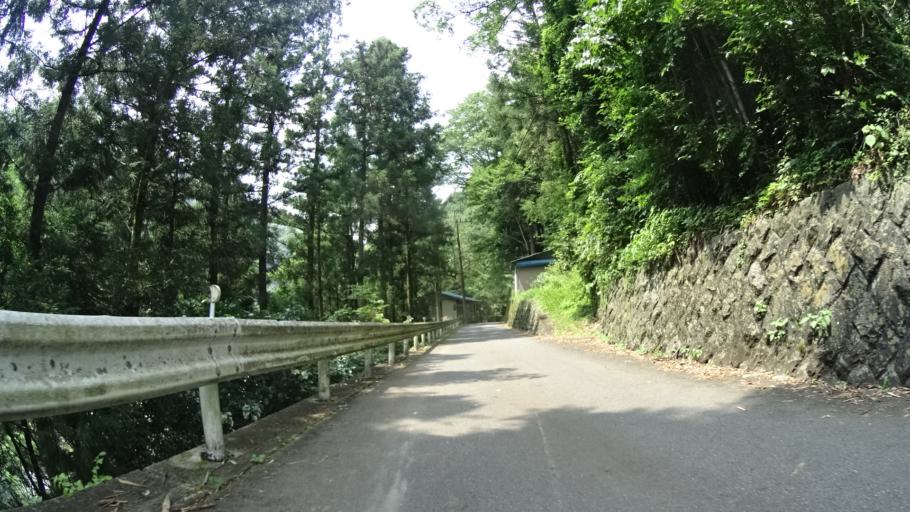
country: JP
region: Gunma
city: Tomioka
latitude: 36.0846
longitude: 138.7204
